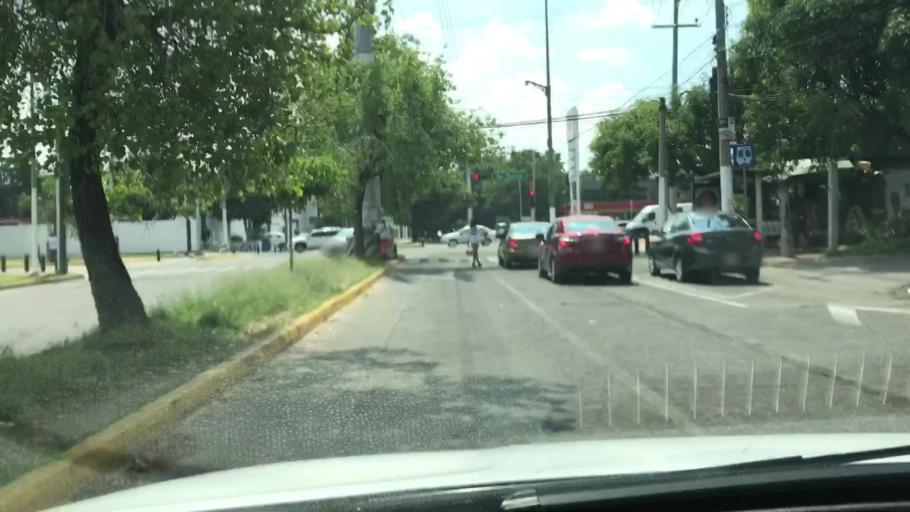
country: MX
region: Jalisco
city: Guadalajara
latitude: 20.6501
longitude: -103.4220
